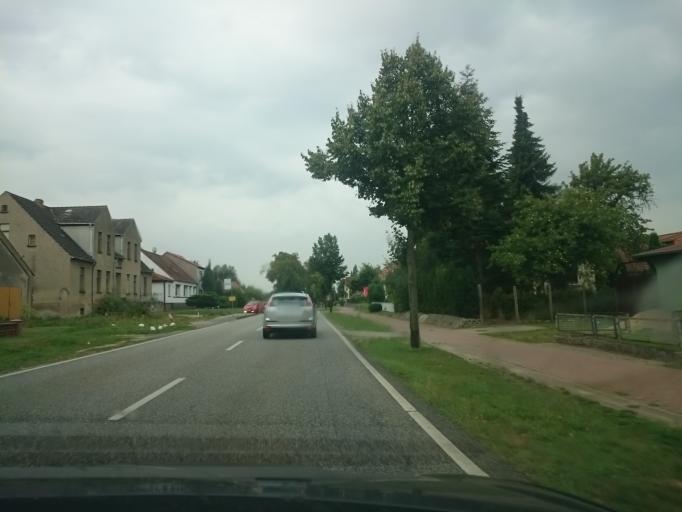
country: DE
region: Brandenburg
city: Gransee
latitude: 53.0328
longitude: 13.1919
